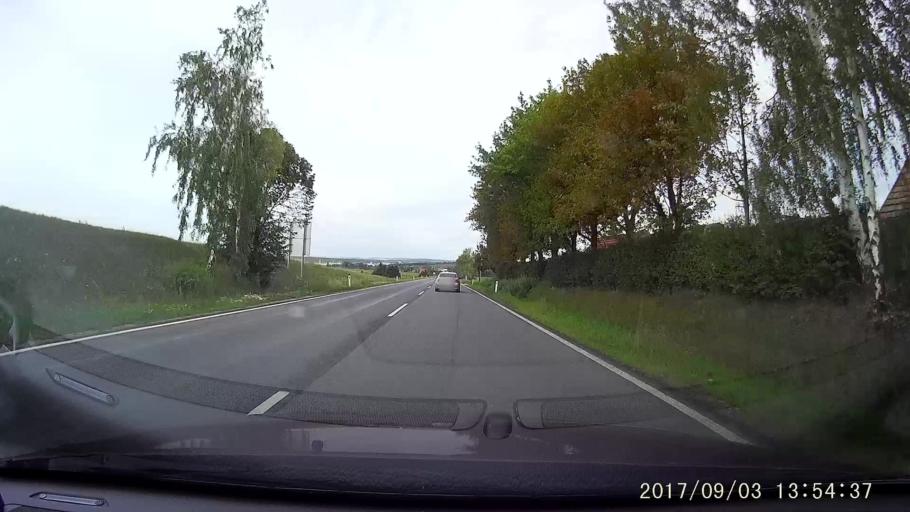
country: AT
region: Lower Austria
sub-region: Politischer Bezirk Hollabrunn
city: Haugsdorf
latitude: 48.7445
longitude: 16.0612
